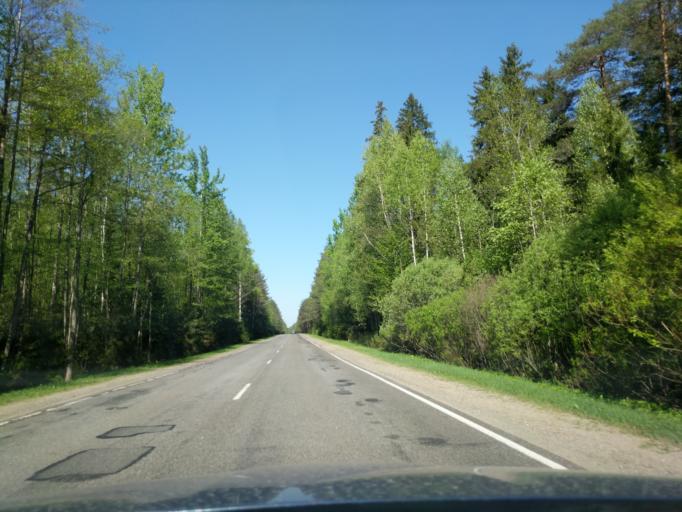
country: BY
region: Minsk
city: Il'ya
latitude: 54.4044
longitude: 27.3200
